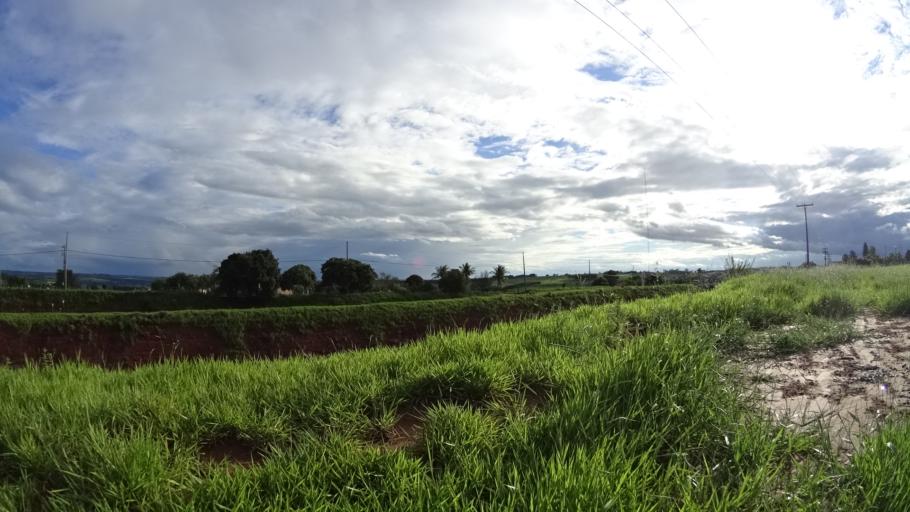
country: BR
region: Sao Paulo
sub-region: Marilia
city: Marilia
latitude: -22.2218
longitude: -49.8795
